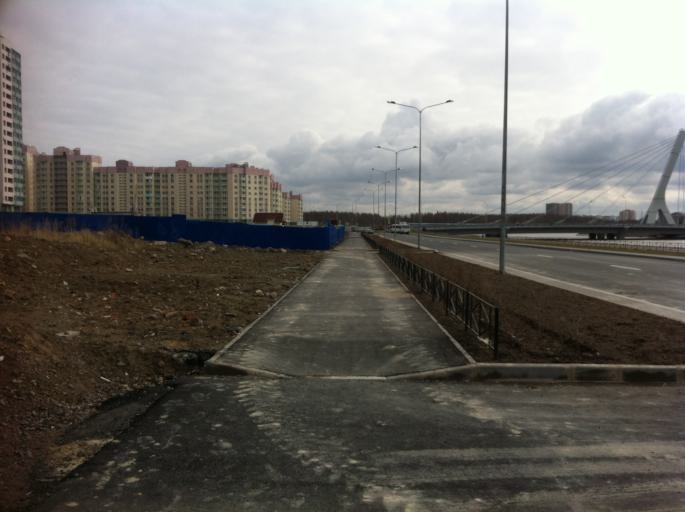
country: RU
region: St.-Petersburg
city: Sosnovaya Polyana
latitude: 59.8617
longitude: 30.1545
